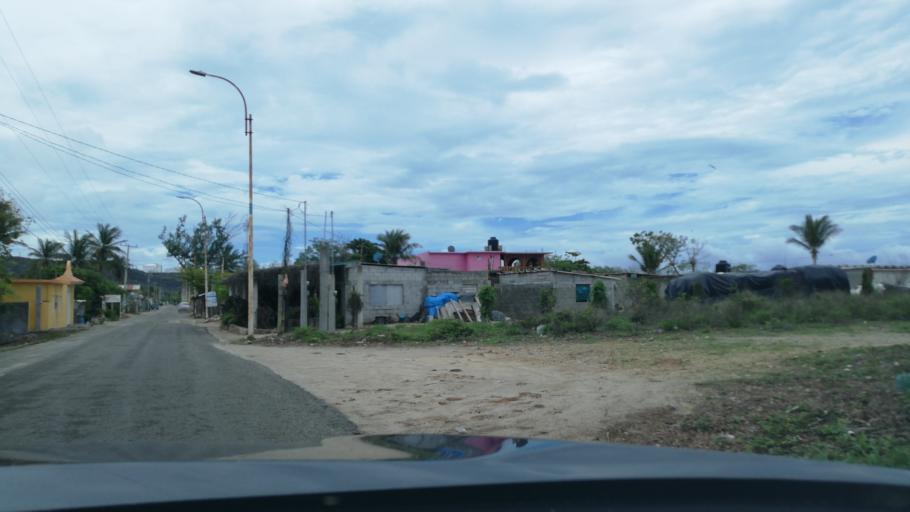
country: MX
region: Oaxaca
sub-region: Salina Cruz
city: Salina Cruz
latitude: 16.1623
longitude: -95.2263
